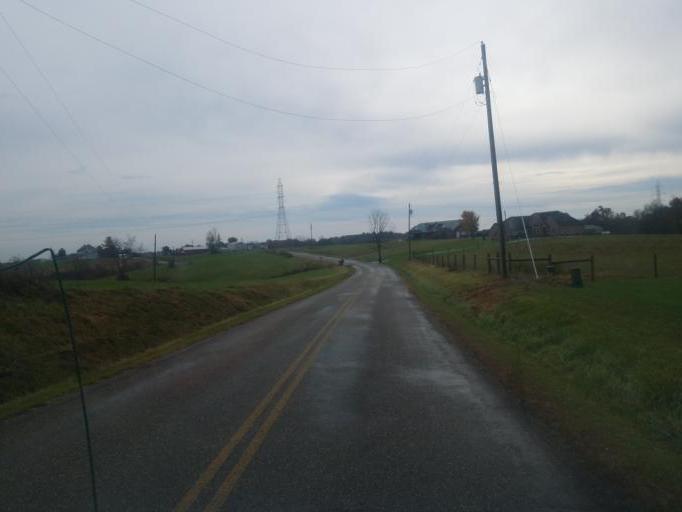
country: US
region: Ohio
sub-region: Washington County
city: Beverly
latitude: 39.5545
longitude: -81.6959
